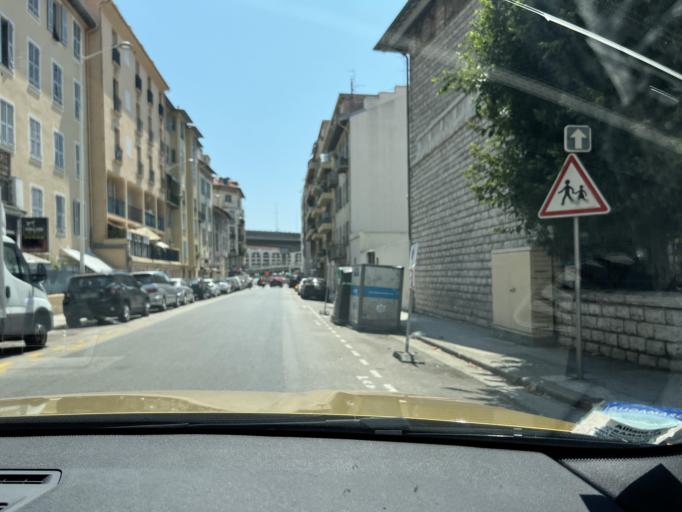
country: FR
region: Provence-Alpes-Cote d'Azur
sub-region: Departement des Alpes-Maritimes
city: Nice
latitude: 43.7071
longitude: 7.2598
